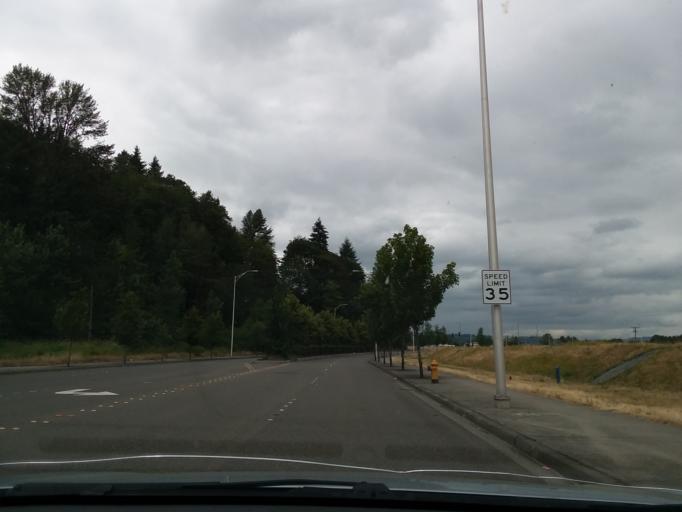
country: US
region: Washington
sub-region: King County
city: SeaTac
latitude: 47.4356
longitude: -122.2645
